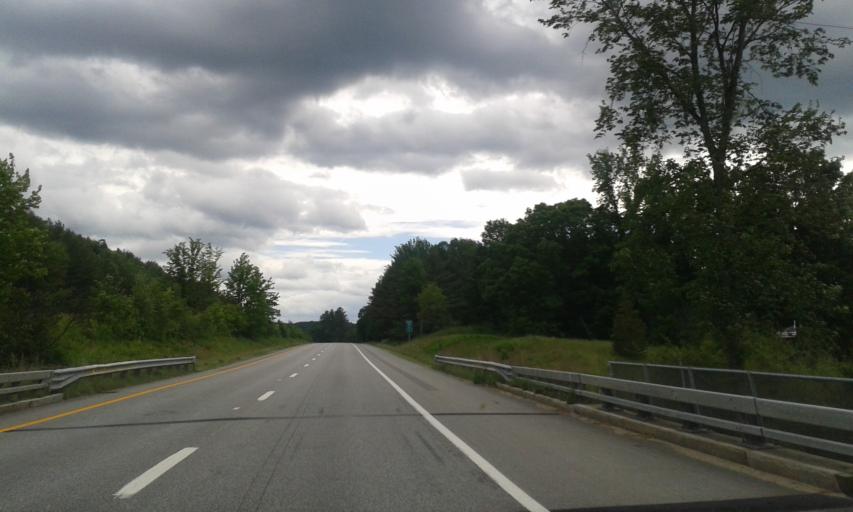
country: US
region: New Hampshire
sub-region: Belknap County
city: Tilton
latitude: 43.4384
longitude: -71.5810
